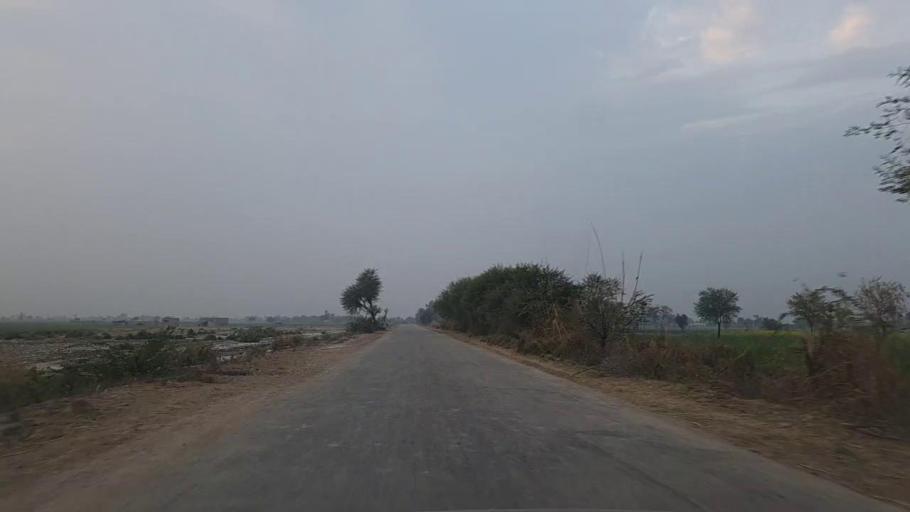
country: PK
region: Sindh
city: Jam Sahib
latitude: 26.3200
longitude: 68.5573
